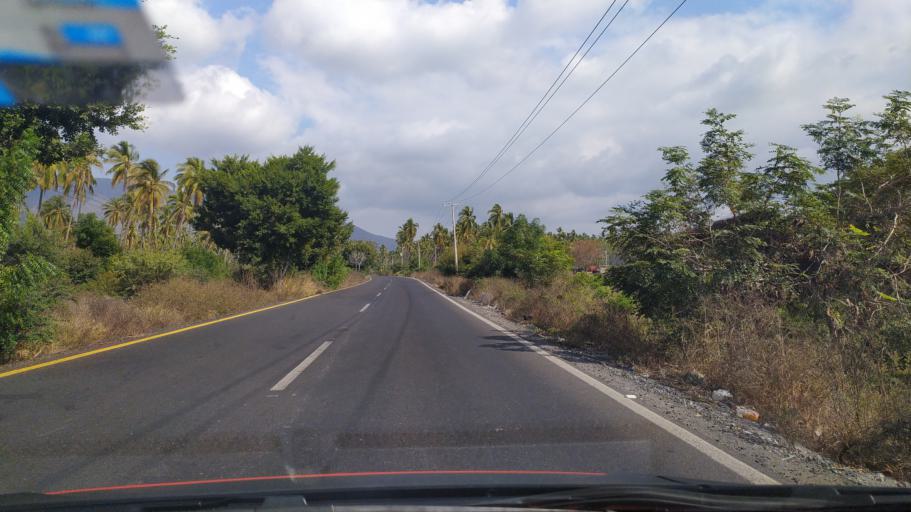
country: MX
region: Colima
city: Tecoman
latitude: 18.9332
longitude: -103.8649
